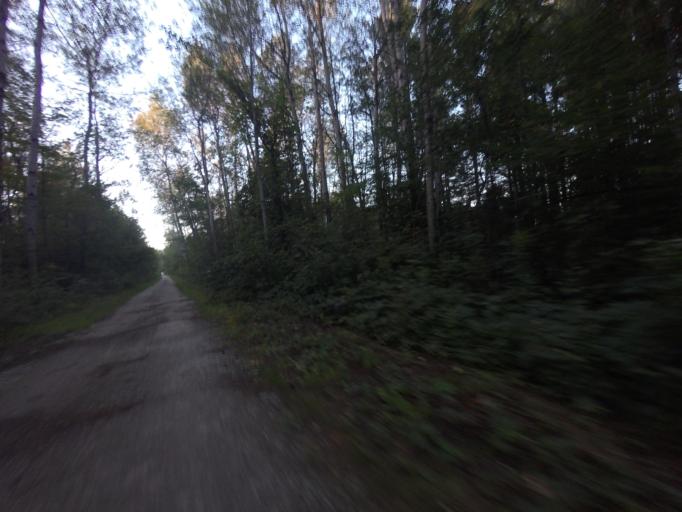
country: CA
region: Ontario
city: Brampton
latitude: 43.9211
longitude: -79.8417
